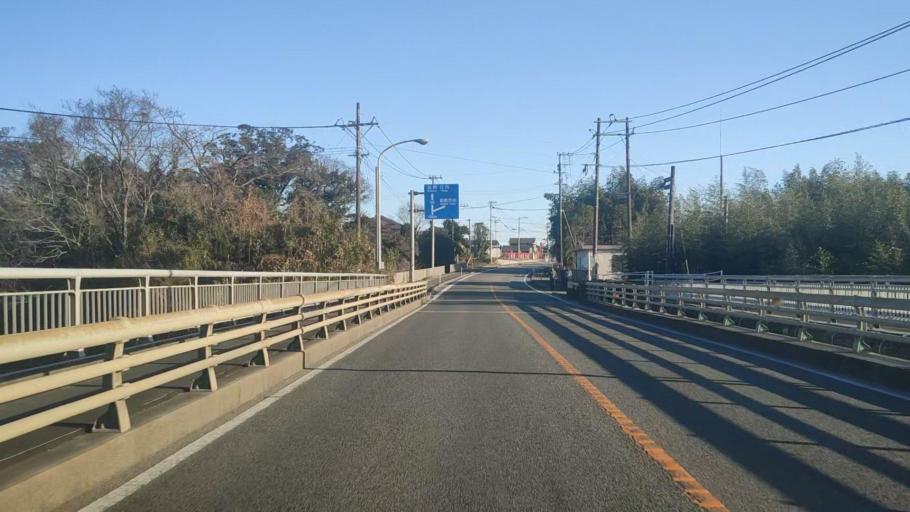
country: JP
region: Miyazaki
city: Takanabe
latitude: 32.2412
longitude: 131.5490
